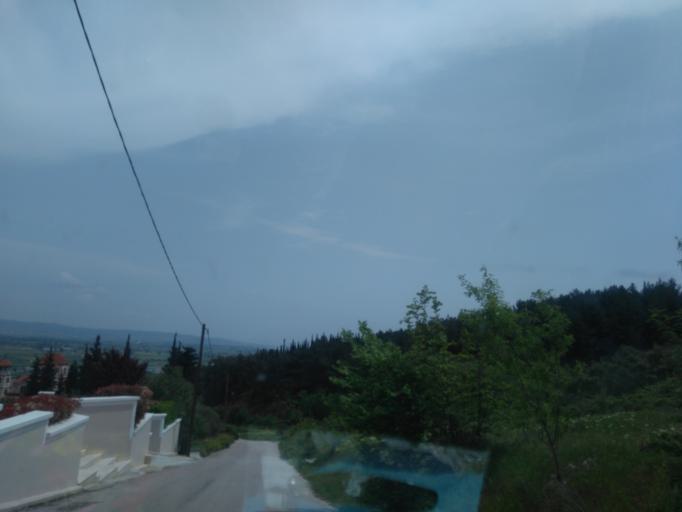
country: GR
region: Central Macedonia
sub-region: Nomos Thessalonikis
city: Lagyna
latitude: 40.7221
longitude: 22.9988
